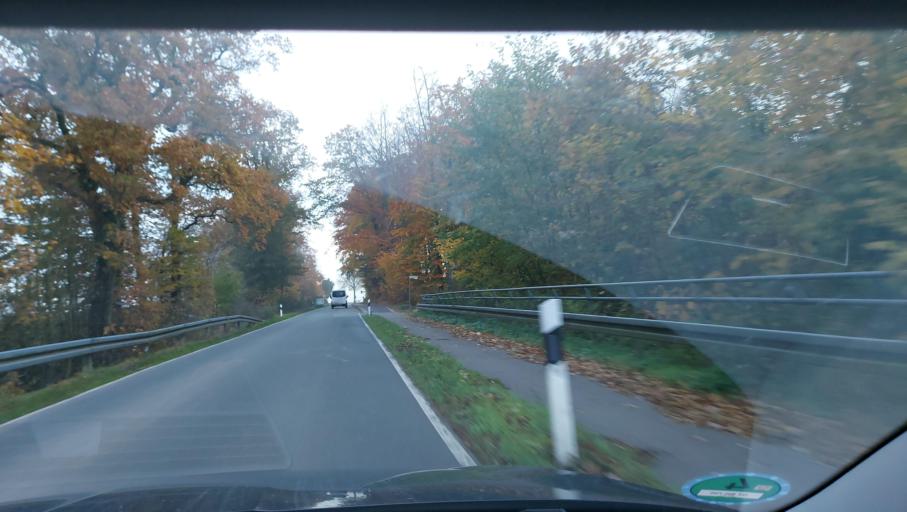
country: DE
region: Lower Saxony
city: Neuenkirchen
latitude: 52.1467
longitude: 8.4147
